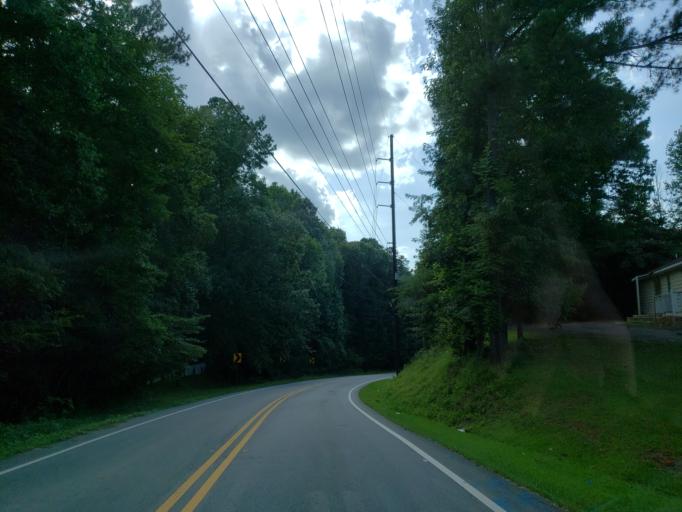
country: US
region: Georgia
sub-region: Cobb County
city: Powder Springs
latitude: 33.8738
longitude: -84.6404
